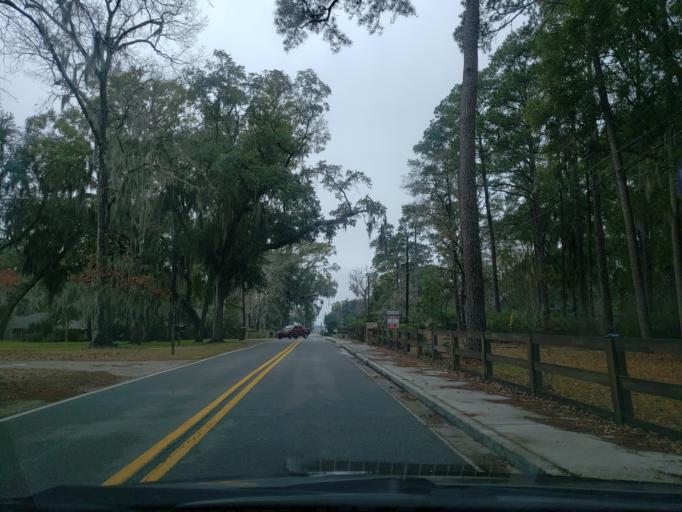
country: US
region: Georgia
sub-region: Chatham County
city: Montgomery
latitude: 31.9384
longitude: -81.1523
